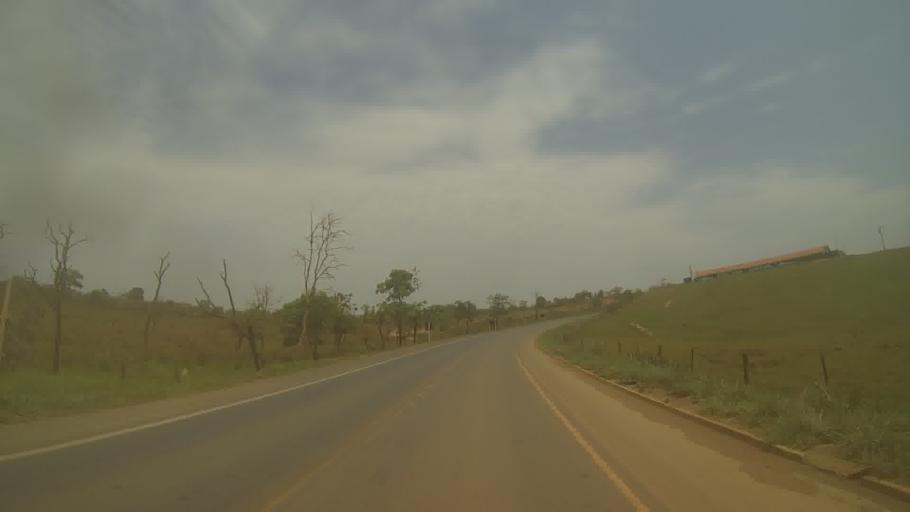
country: BR
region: Minas Gerais
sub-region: Bambui
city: Bambui
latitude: -20.0157
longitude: -45.9394
